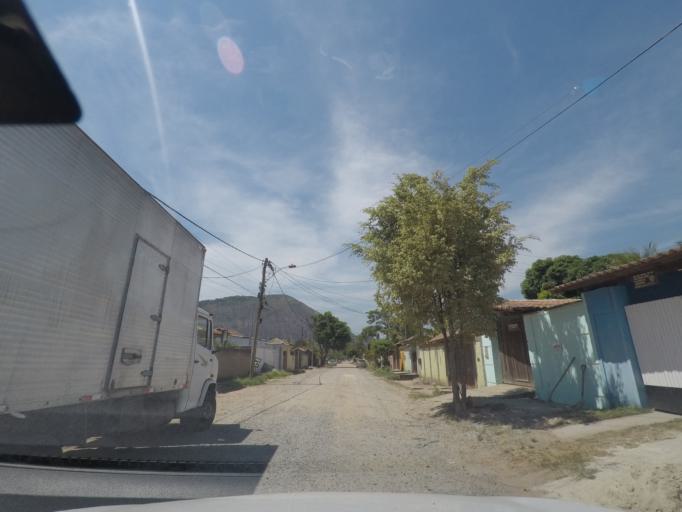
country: BR
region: Rio de Janeiro
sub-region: Marica
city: Marica
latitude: -22.9563
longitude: -42.9577
